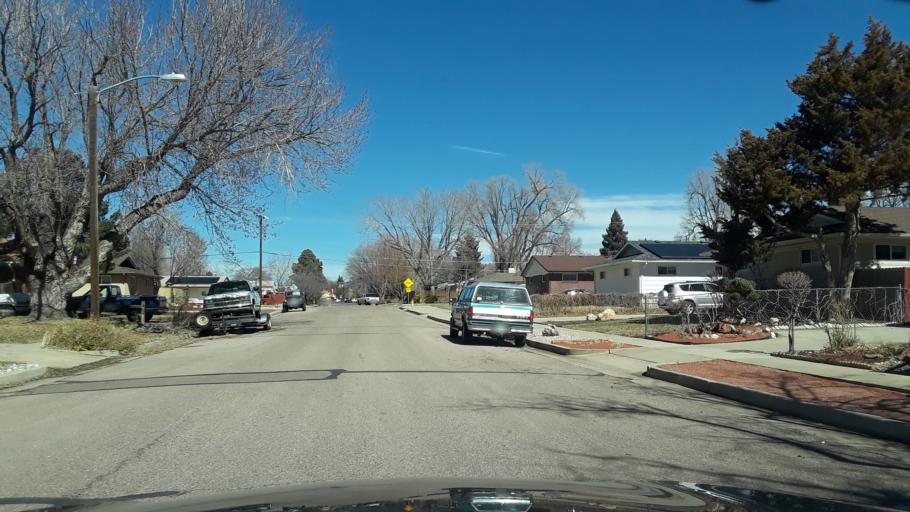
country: US
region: Colorado
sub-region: El Paso County
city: Colorado Springs
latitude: 38.8711
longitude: -104.8056
